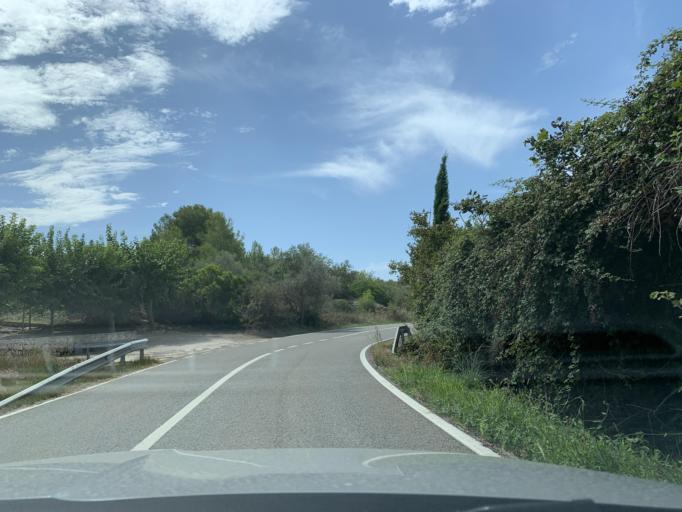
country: ES
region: Catalonia
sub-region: Provincia de Tarragona
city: Altafulla
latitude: 41.1644
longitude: 1.3672
